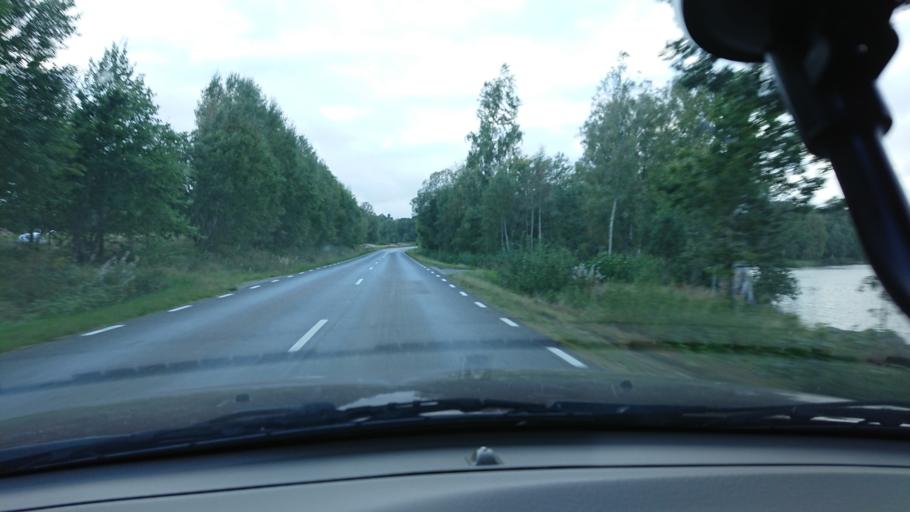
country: SE
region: Kronoberg
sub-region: Vaxjo Kommun
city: Lammhult
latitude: 57.0681
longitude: 14.7287
